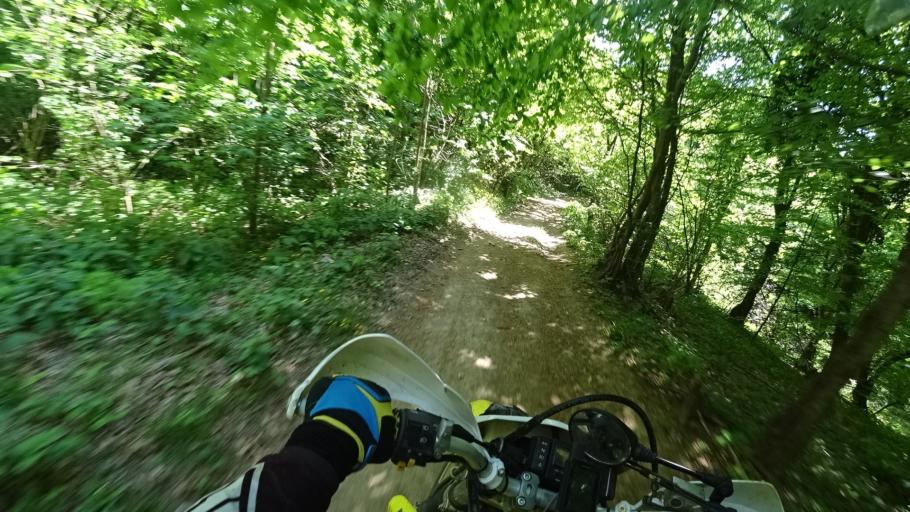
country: HR
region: Zagrebacka
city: Jablanovec
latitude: 45.8526
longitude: 15.8575
